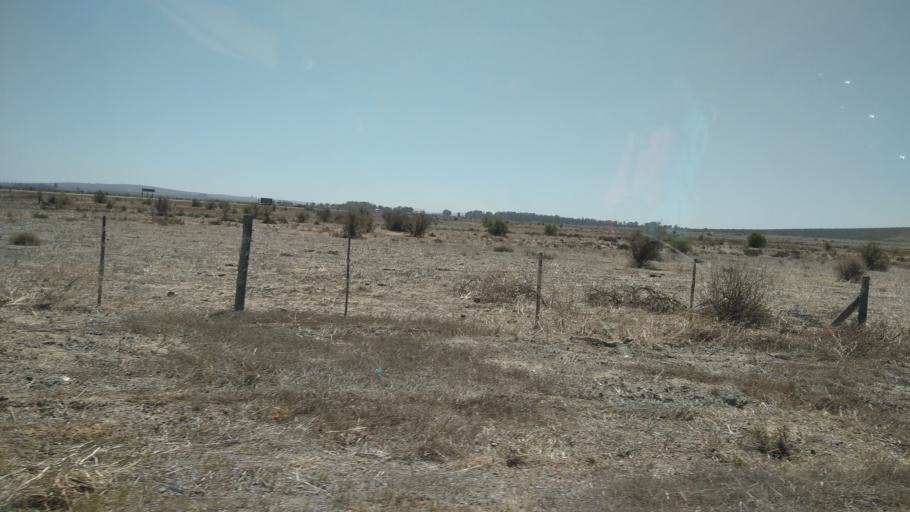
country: ZA
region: Western Cape
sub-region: West Coast District Municipality
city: Saldanha
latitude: -33.0243
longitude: 18.1076
